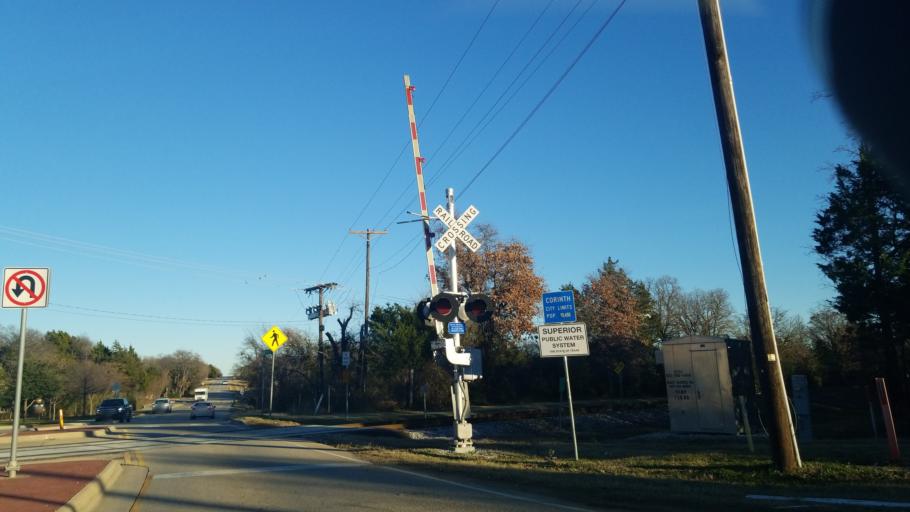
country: US
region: Texas
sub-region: Denton County
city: Corinth
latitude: 33.1632
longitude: -97.0686
